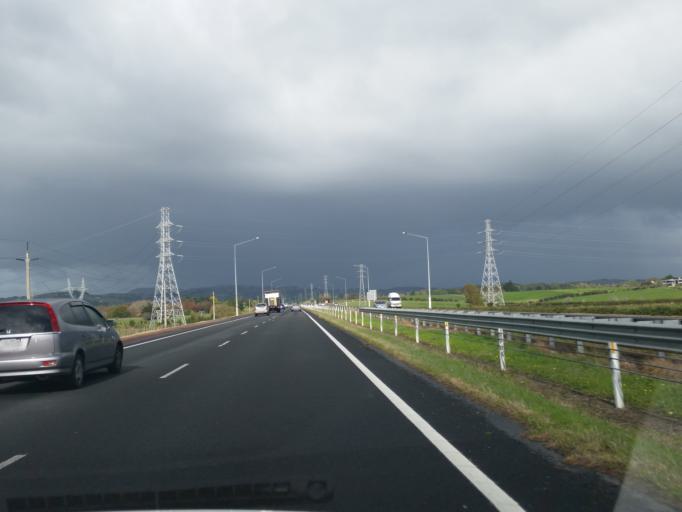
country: NZ
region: Auckland
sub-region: Auckland
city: Papakura
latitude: -37.1230
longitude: 174.9576
